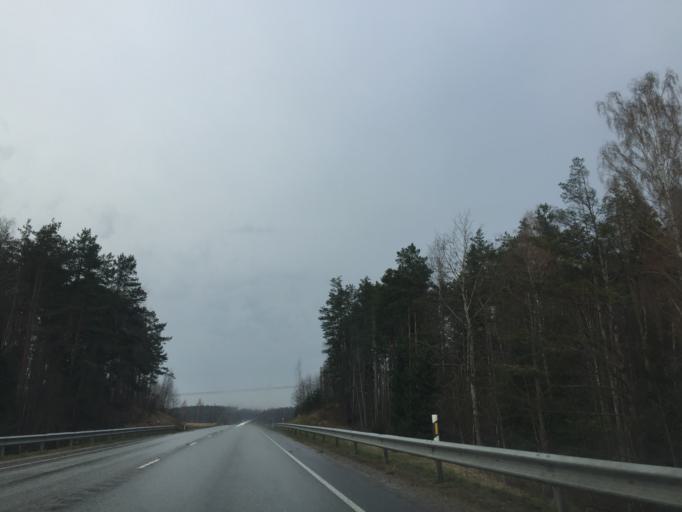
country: EE
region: Tartu
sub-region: UElenurme vald
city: Ulenurme
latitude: 58.2126
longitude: 26.7057
